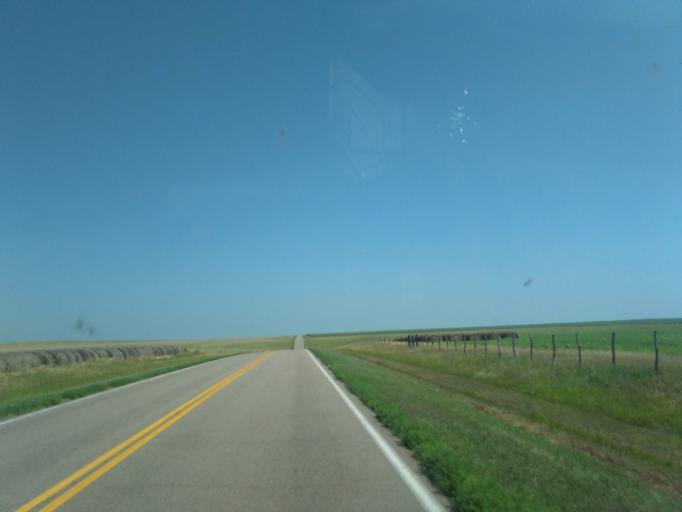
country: US
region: Nebraska
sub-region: Dundy County
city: Benkelman
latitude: 39.9094
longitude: -101.5412
